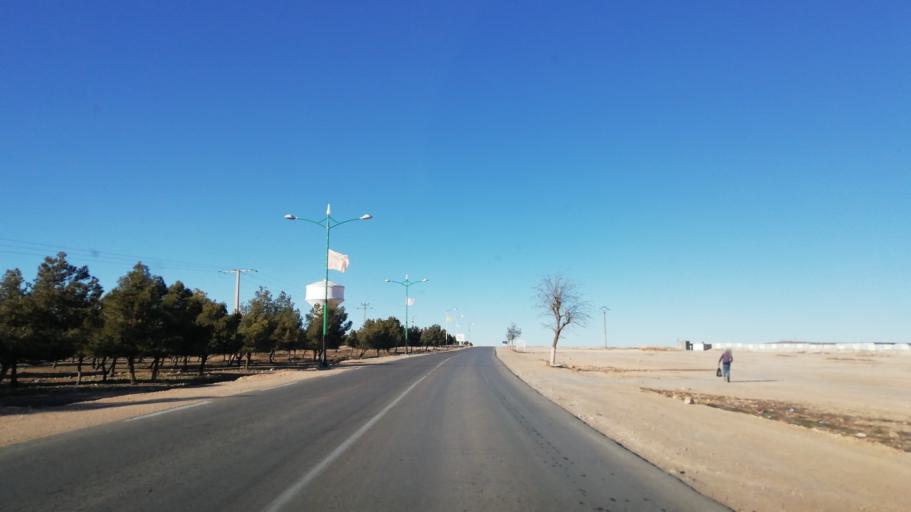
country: DZ
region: Tlemcen
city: Sebdou
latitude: 34.2288
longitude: -1.2562
